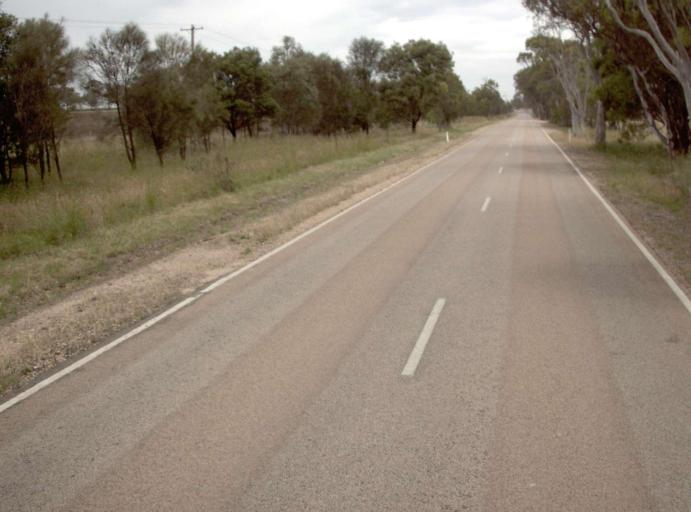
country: AU
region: Victoria
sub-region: East Gippsland
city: Bairnsdale
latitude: -37.8755
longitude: 147.4238
